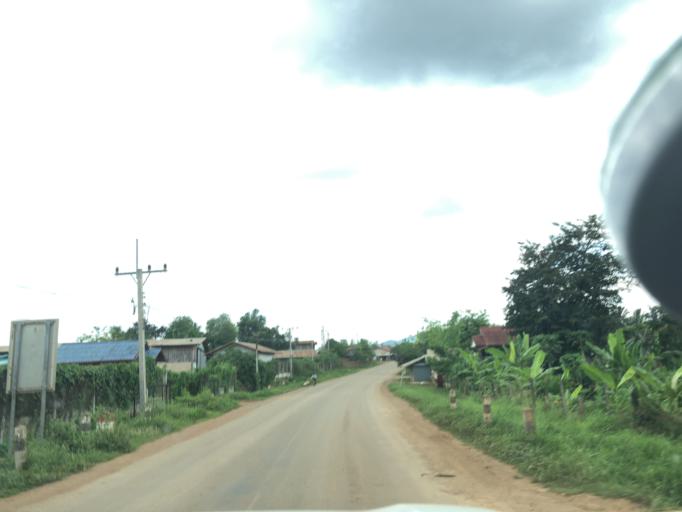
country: TH
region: Uttaradit
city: Ban Khok
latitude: 18.1113
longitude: 101.3726
